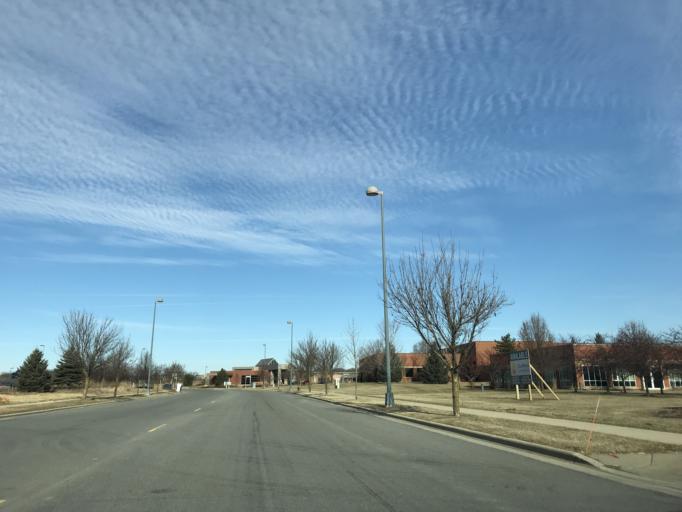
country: US
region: Wisconsin
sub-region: Dane County
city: Windsor
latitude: 43.1493
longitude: -89.2938
